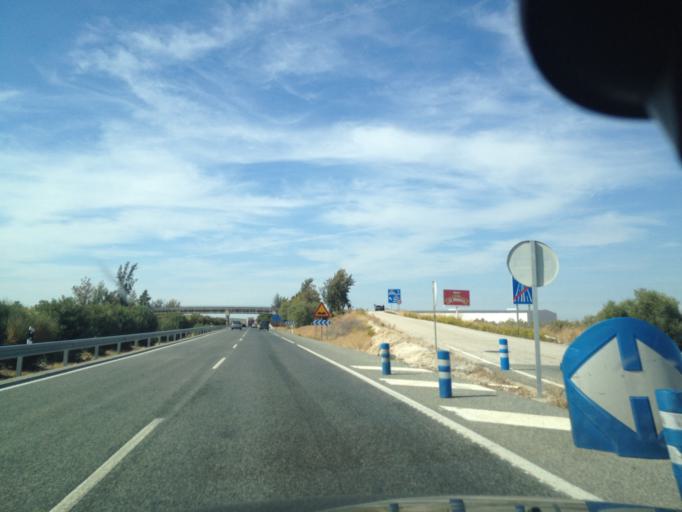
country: ES
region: Andalusia
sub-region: Provincia de Sevilla
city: Osuna
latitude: 37.2339
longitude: -5.1614
